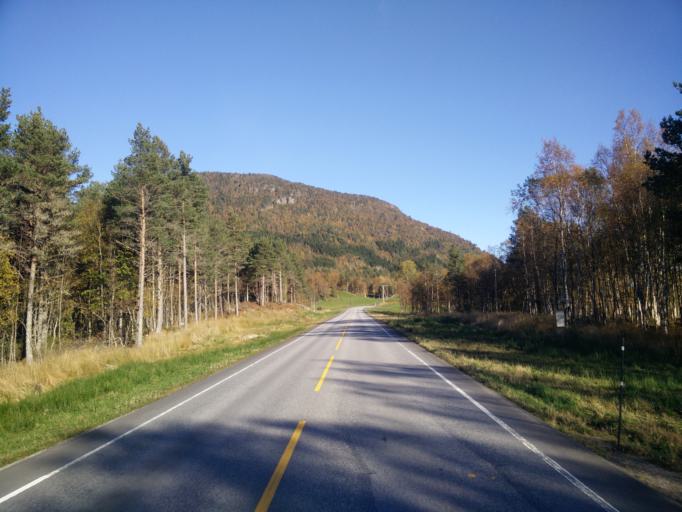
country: NO
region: More og Romsdal
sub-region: Tingvoll
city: Tingvoll
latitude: 63.0467
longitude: 8.0738
